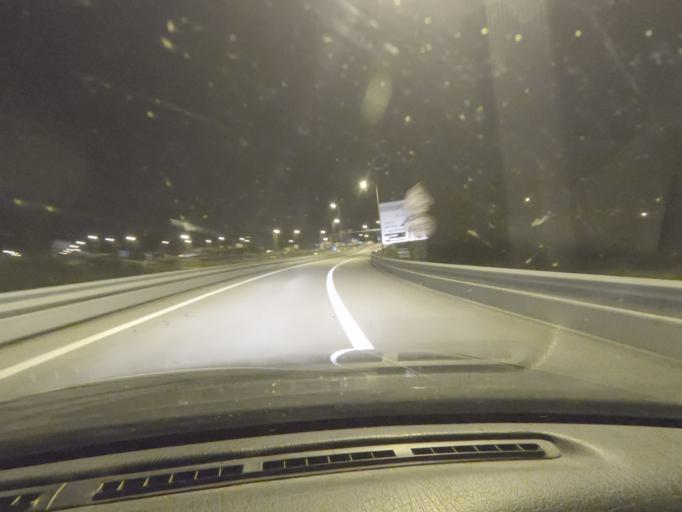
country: PT
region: Vila Real
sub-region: Vila Real
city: Vila Real
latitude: 41.2819
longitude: -7.7186
